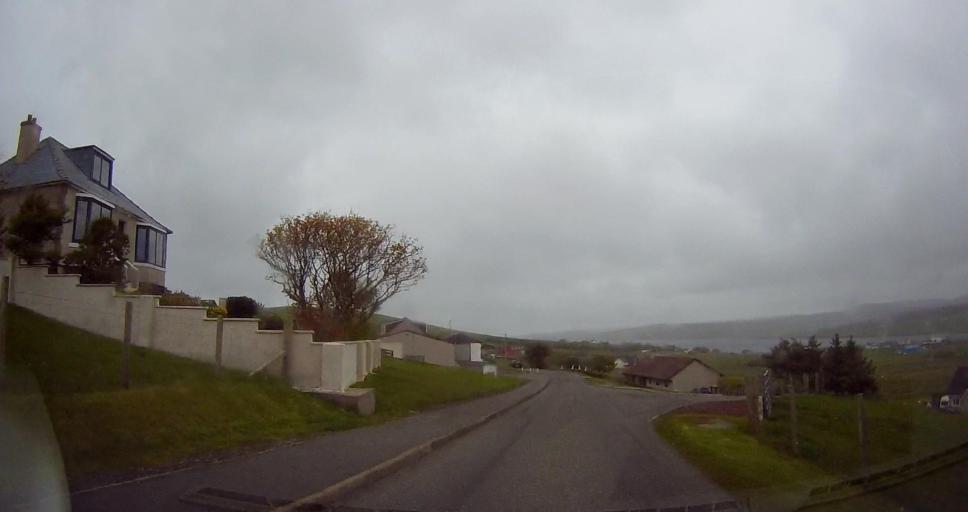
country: GB
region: Scotland
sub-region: Shetland Islands
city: Lerwick
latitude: 60.2797
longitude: -1.3890
